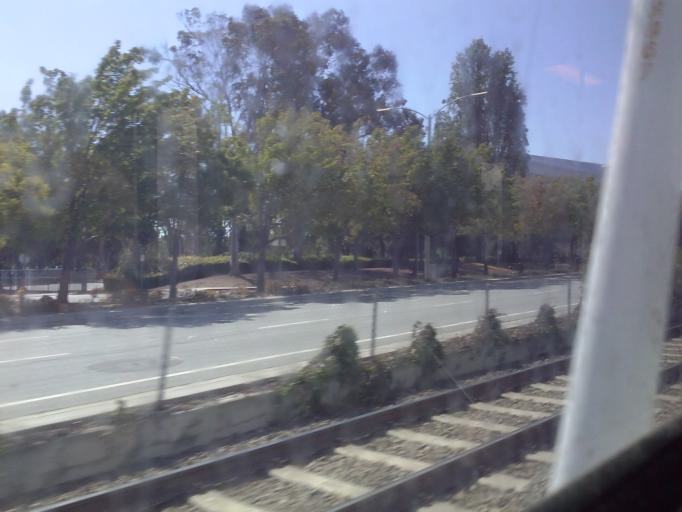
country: US
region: California
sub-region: Santa Clara County
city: Sunnyvale
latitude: 37.4124
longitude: -122.0261
